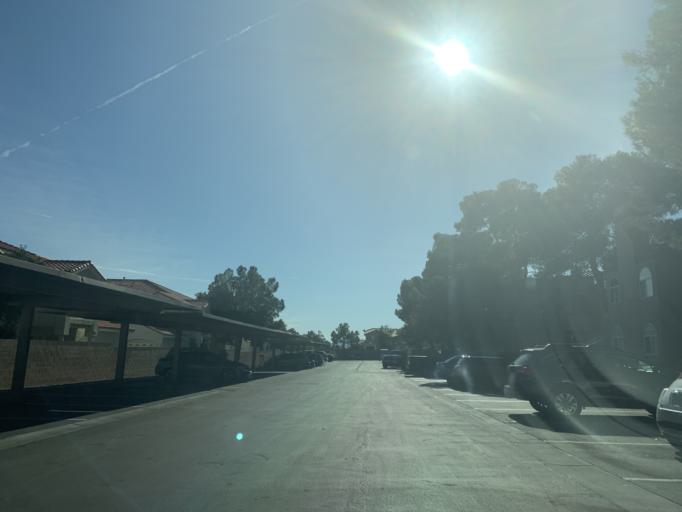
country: US
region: Nevada
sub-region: Clark County
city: Summerlin South
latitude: 36.1289
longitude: -115.2938
